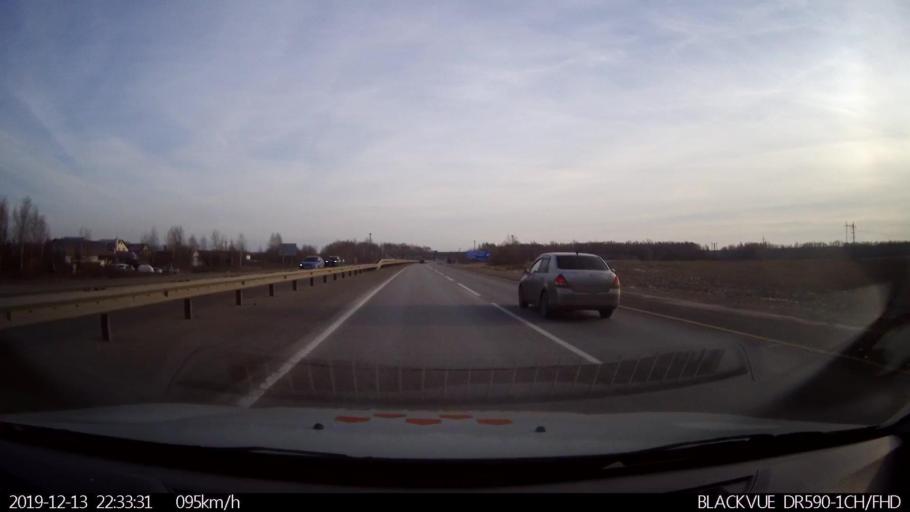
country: RU
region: Nizjnij Novgorod
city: Afonino
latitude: 56.1968
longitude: 44.1158
